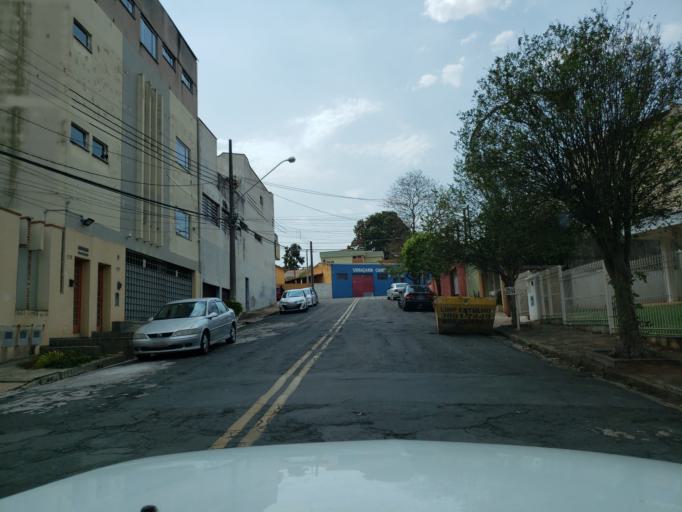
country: BR
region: Sao Paulo
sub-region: Moji-Guacu
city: Mogi-Gaucu
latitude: -22.3651
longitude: -46.9447
